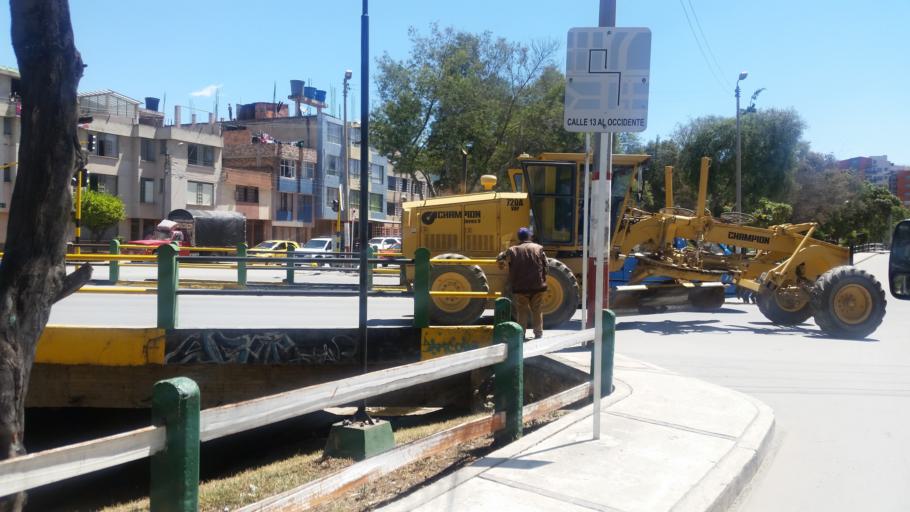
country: CO
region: Boyaca
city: Sogamoso
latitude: 5.7208
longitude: -72.9322
